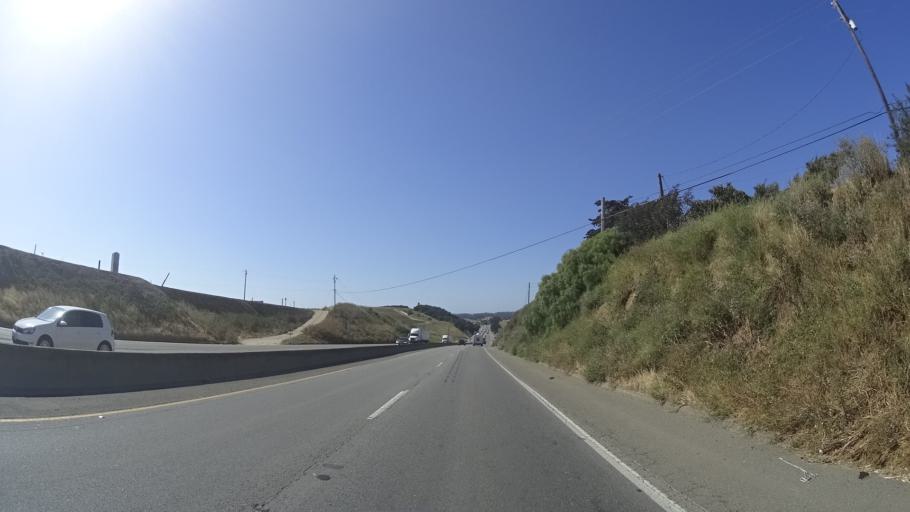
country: US
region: California
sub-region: Monterey County
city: Prunedale
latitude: 36.7525
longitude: -121.6638
